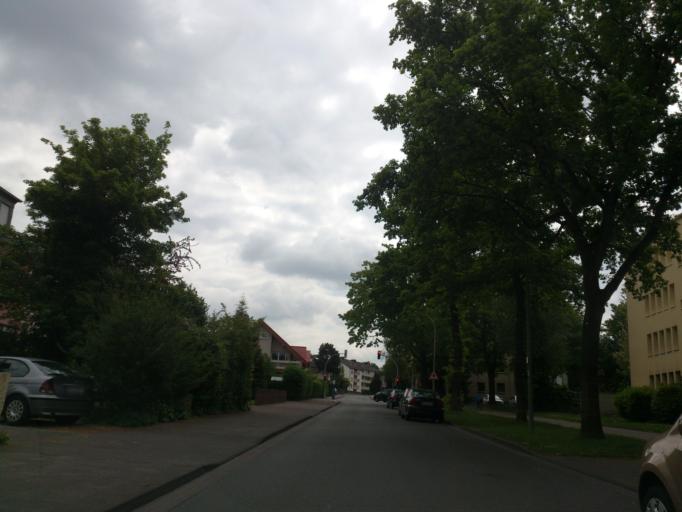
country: DE
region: North Rhine-Westphalia
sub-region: Regierungsbezirk Detmold
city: Paderborn
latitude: 51.7064
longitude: 8.7589
